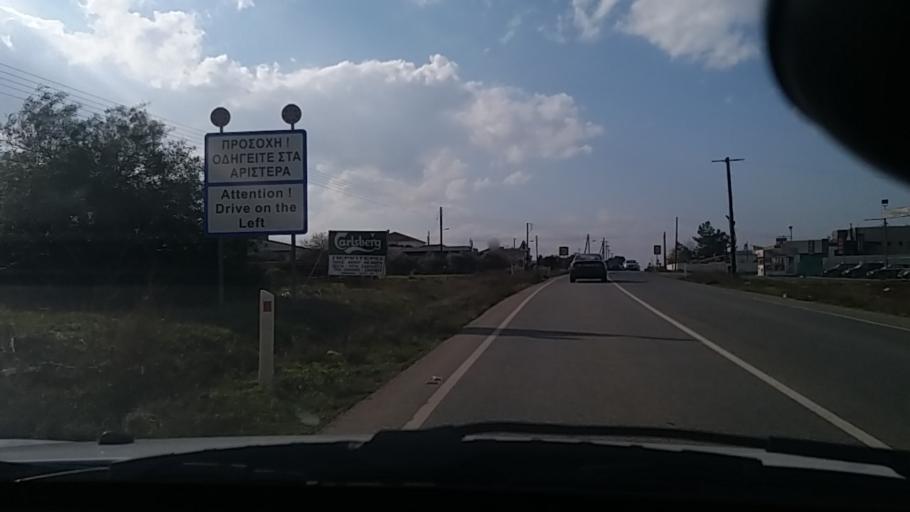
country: CY
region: Lefkosia
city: Akaki
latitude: 35.1374
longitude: 33.1515
